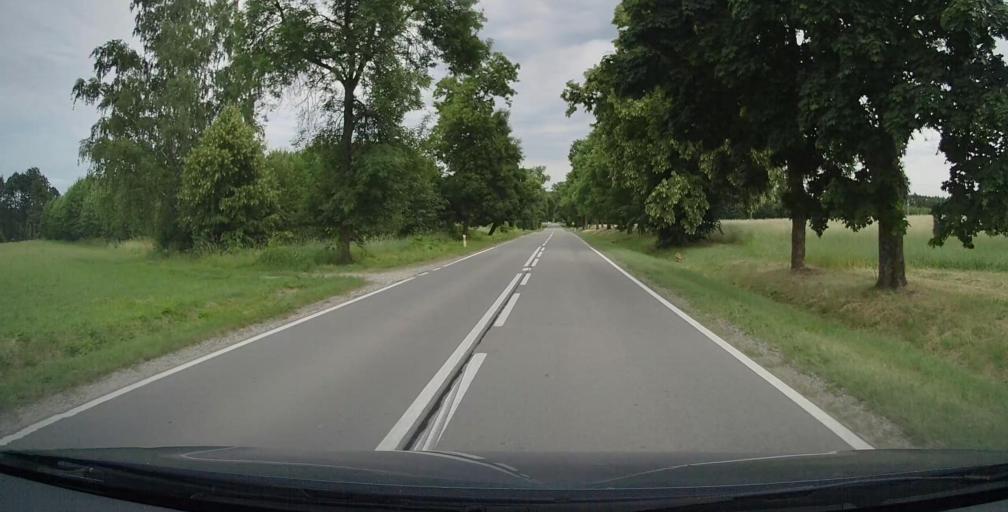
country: PL
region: Masovian Voivodeship
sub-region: Powiat losicki
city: Sarnaki
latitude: 52.3076
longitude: 22.9383
